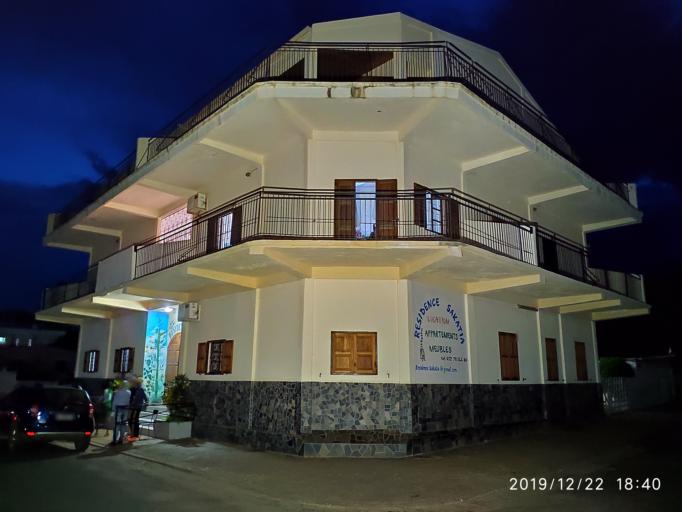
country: MG
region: Diana
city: Antsiranana
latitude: -12.2718
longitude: 49.2937
